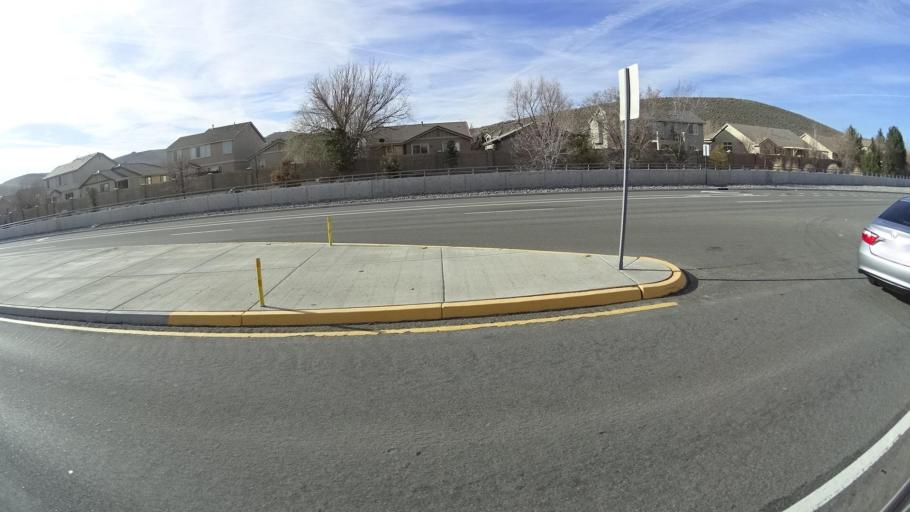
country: US
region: Nevada
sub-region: Washoe County
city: Spanish Springs
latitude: 39.6070
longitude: -119.6996
